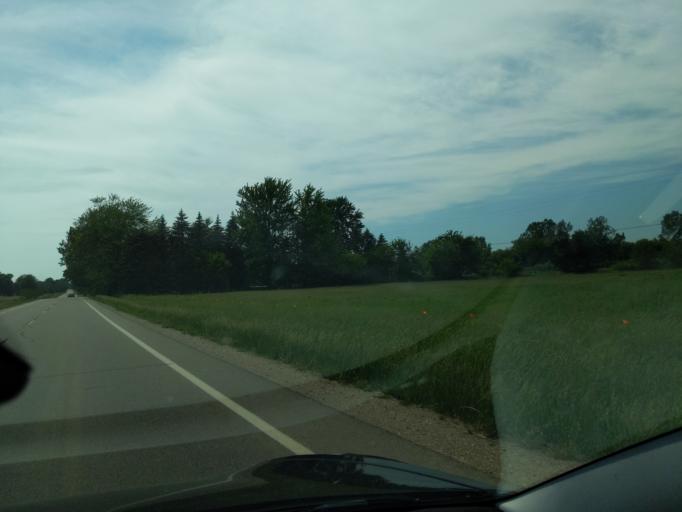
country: US
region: Michigan
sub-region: Eaton County
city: Grand Ledge
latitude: 42.7119
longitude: -84.7828
